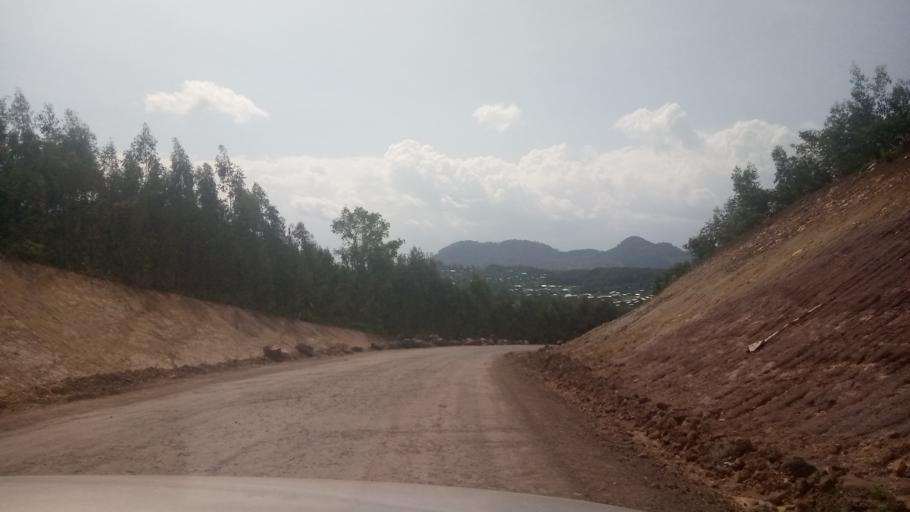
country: ET
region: Oromiya
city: Agaro
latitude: 7.9921
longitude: 36.5048
